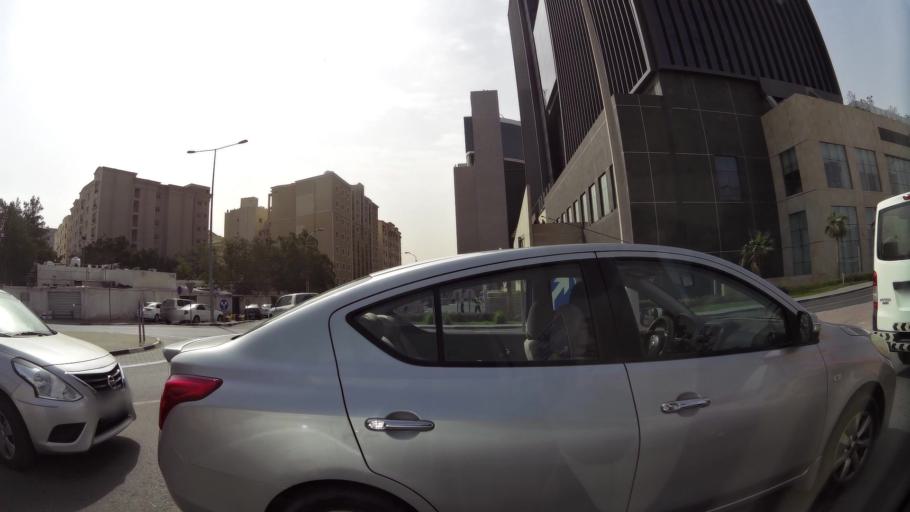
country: QA
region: Baladiyat ad Dawhah
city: Doha
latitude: 25.2820
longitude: 51.5076
